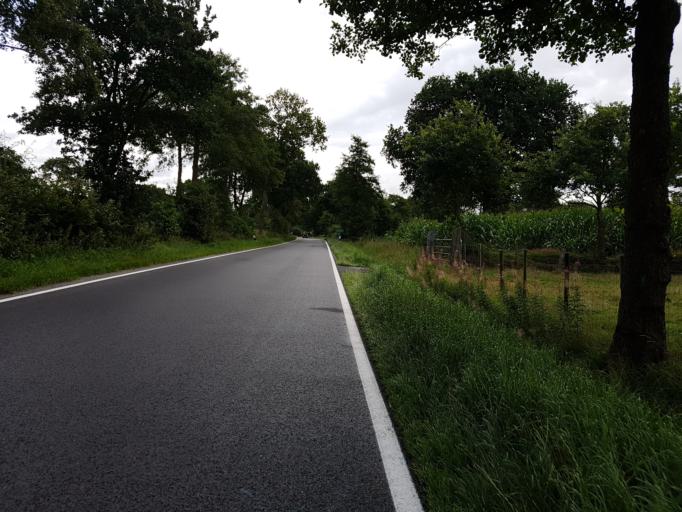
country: DE
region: Lower Saxony
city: Wittmund
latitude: 53.5236
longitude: 7.7208
